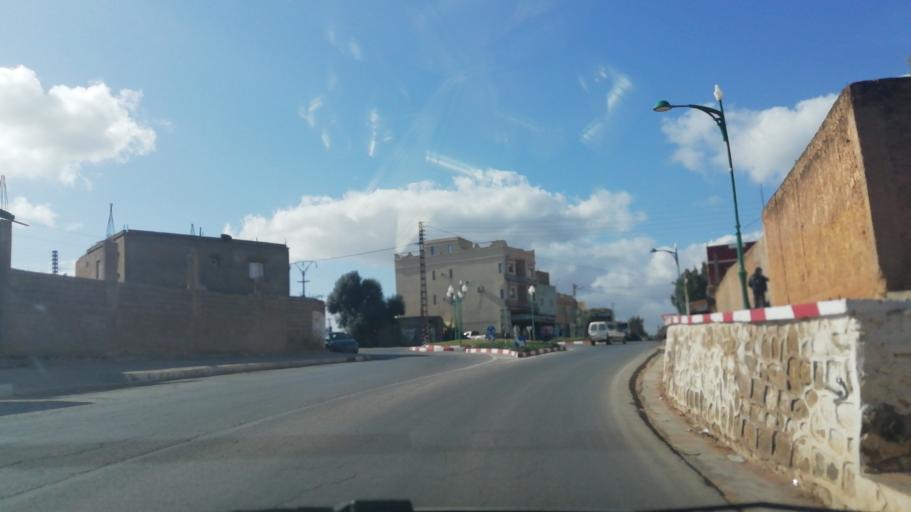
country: DZ
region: Relizane
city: Mazouna
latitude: 36.2834
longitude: 0.6441
